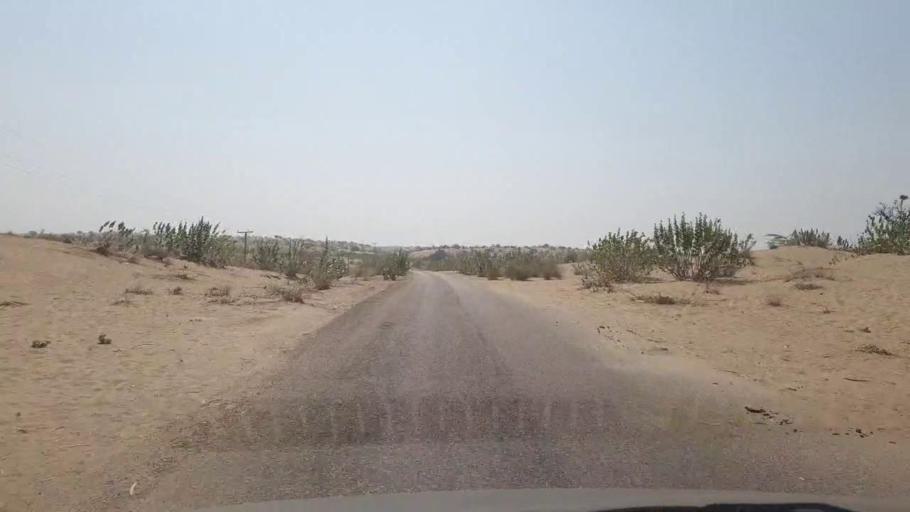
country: PK
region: Sindh
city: Chor
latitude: 25.6624
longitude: 70.1669
